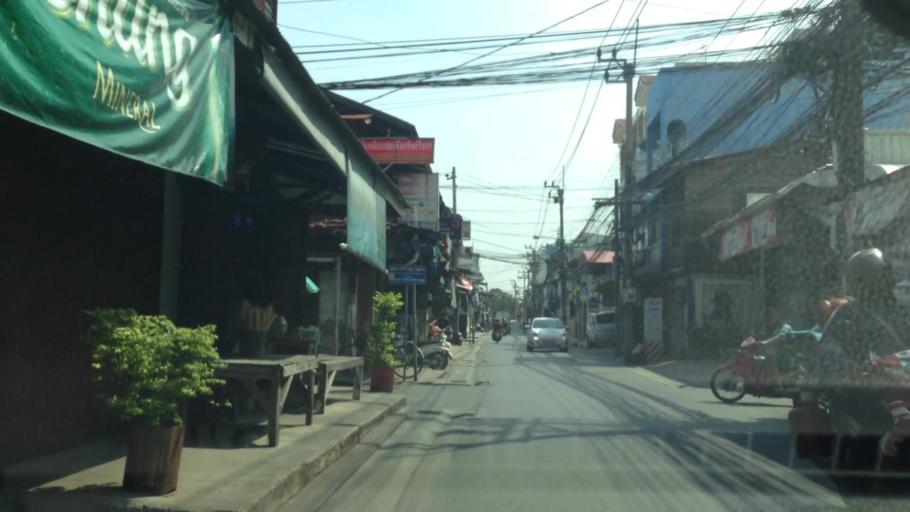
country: TH
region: Bangkok
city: Sai Mai
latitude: 13.9074
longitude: 100.6268
